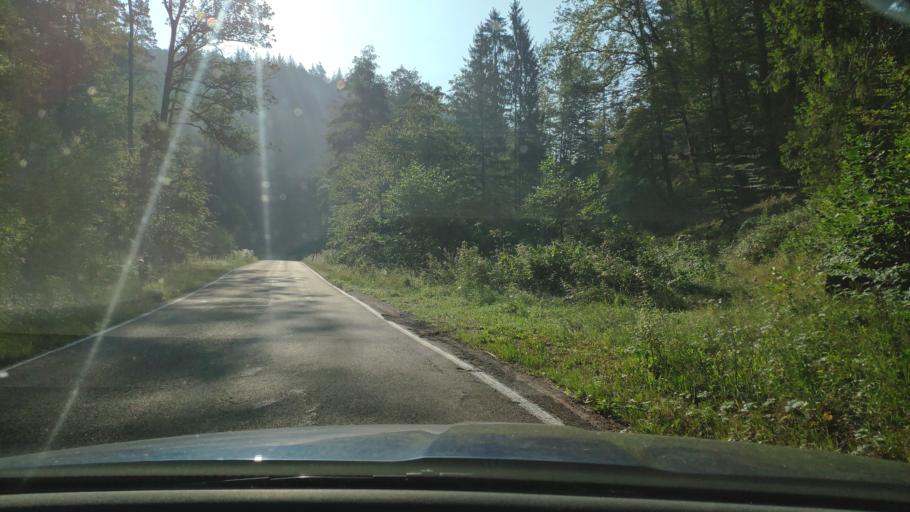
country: DE
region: Rheinland-Pfalz
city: Ludwigswinkel
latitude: 49.0993
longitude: 7.6261
